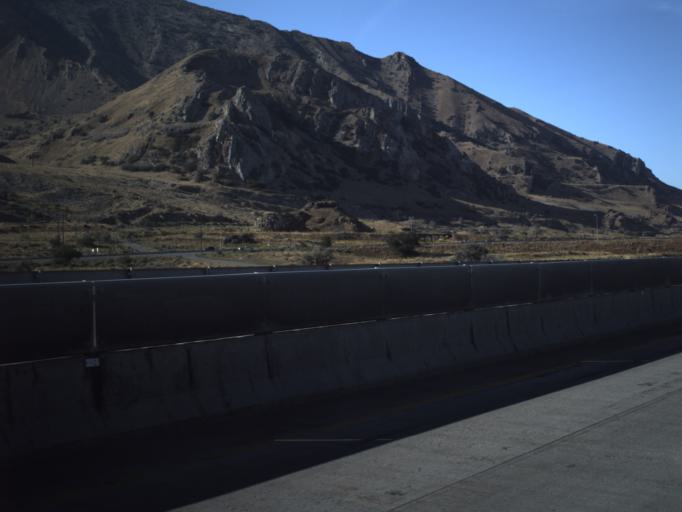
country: US
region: Utah
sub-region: Tooele County
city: Stansbury park
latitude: 40.7255
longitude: -112.2202
